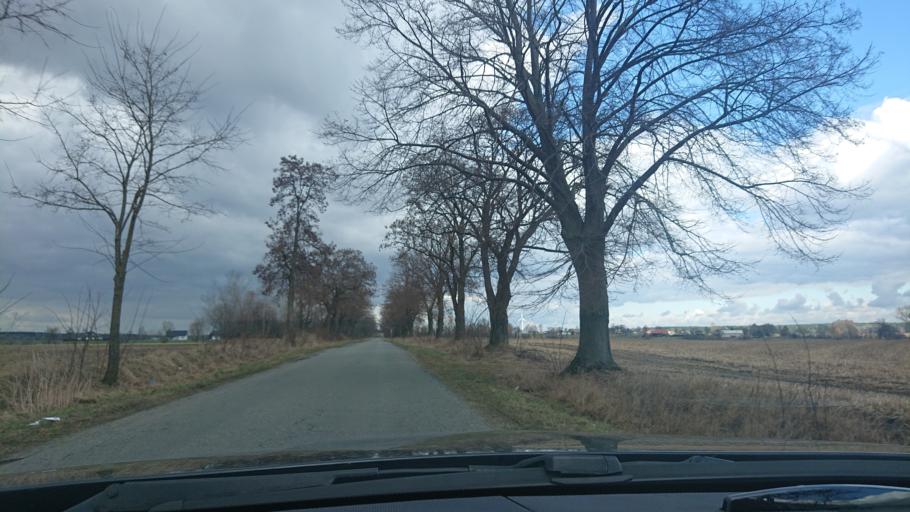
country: PL
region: Greater Poland Voivodeship
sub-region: Powiat gnieznienski
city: Niechanowo
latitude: 52.5768
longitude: 17.7083
